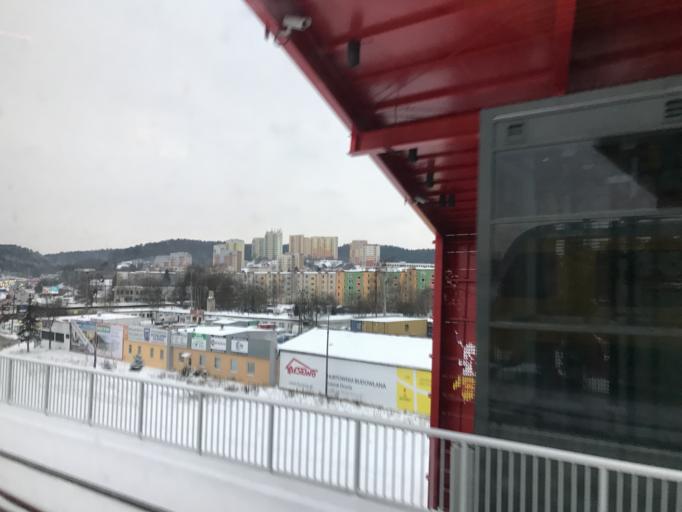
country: PL
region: Pomeranian Voivodeship
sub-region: Sopot
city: Sopot
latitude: 54.3774
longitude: 18.5716
